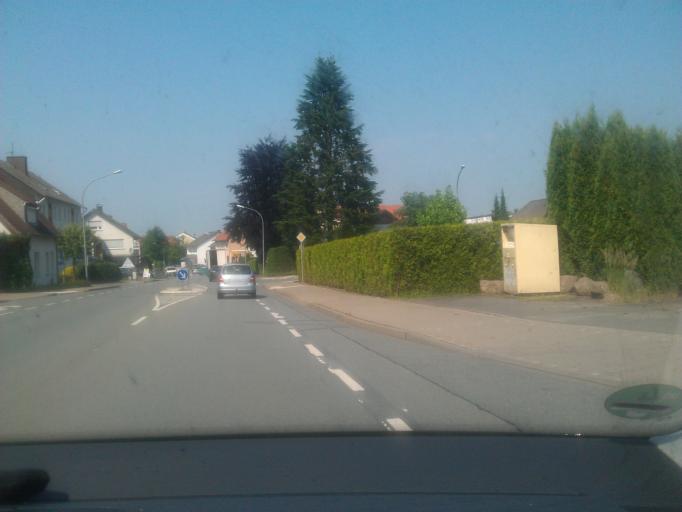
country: DE
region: North Rhine-Westphalia
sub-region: Regierungsbezirk Detmold
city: Oerlinghausen
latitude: 51.9817
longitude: 8.6709
